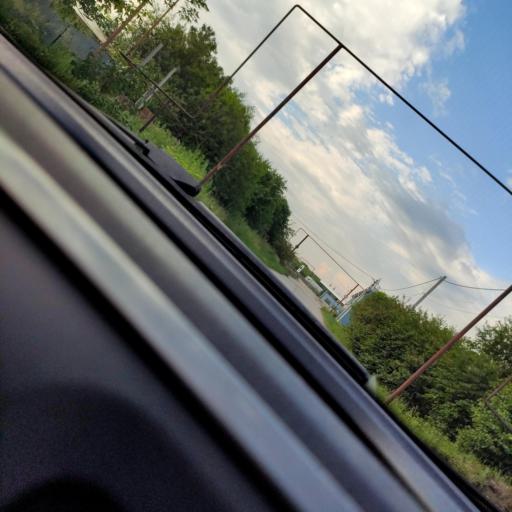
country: RU
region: Samara
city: Tol'yatti
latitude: 53.5700
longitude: 49.3871
